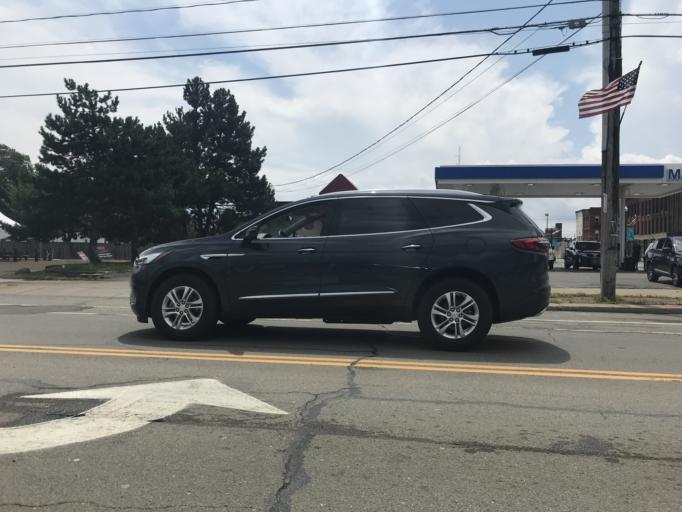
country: US
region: New York
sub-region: Chautauqua County
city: Dunkirk
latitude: 42.4873
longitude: -79.3354
